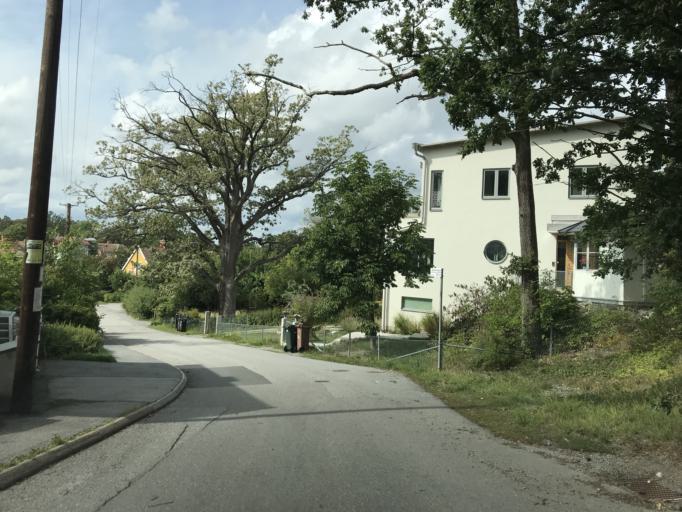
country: SE
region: Stockholm
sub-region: Sundbybergs Kommun
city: Sundbyberg
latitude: 59.3383
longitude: 17.9712
